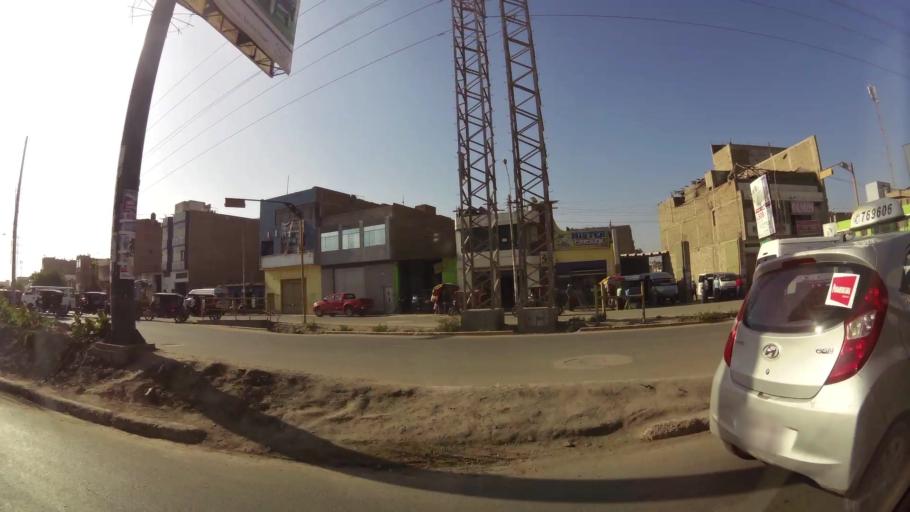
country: PE
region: Lambayeque
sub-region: Provincia de Chiclayo
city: Chiclayo
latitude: -6.7625
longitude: -79.8454
